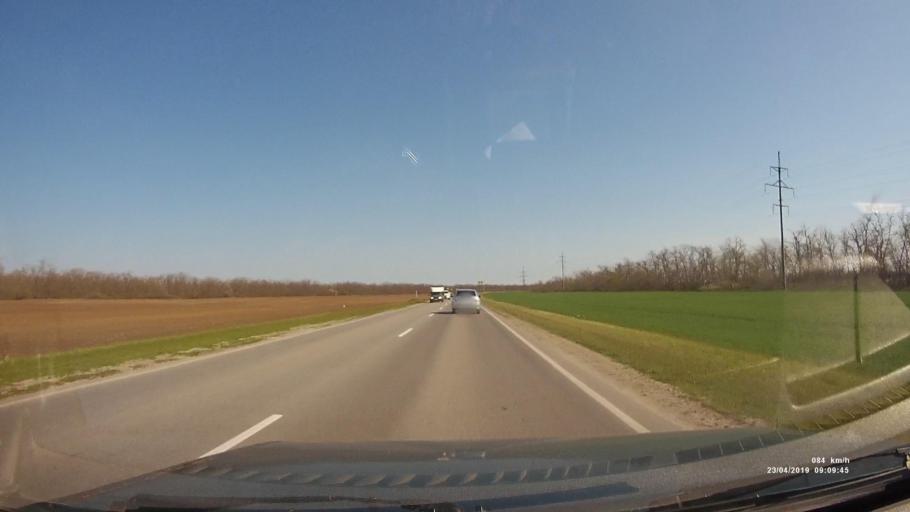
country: RU
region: Rostov
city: Sal'sk
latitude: 46.5777
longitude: 41.6149
